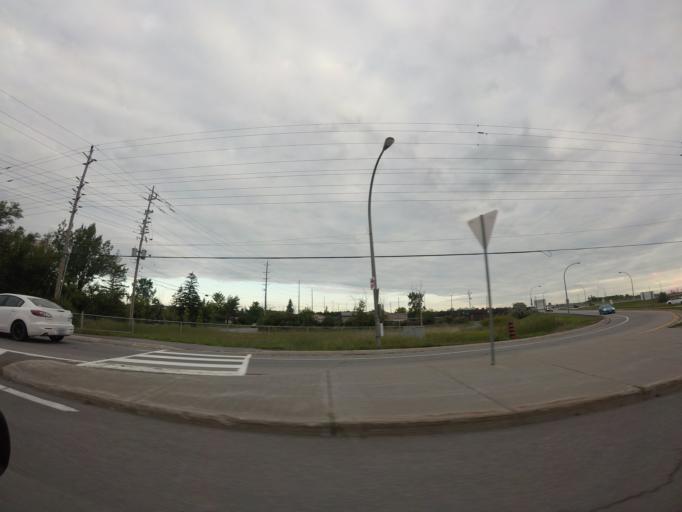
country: CA
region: Quebec
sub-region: Outaouais
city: Gatineau
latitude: 45.4509
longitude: -75.5854
